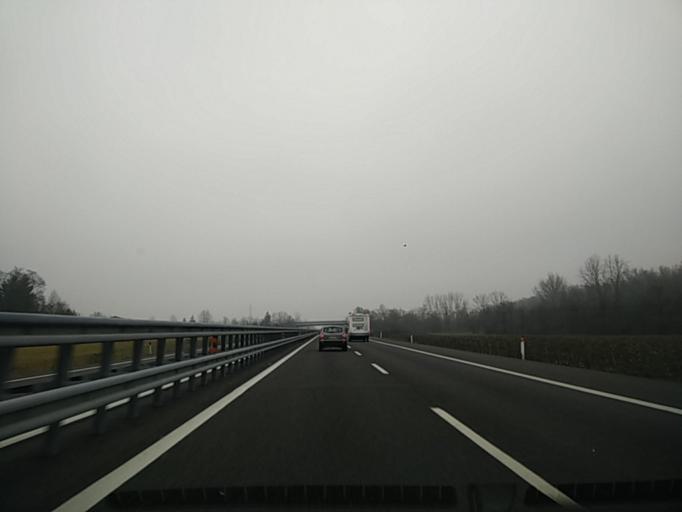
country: IT
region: Piedmont
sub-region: Provincia di Asti
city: Villafranca d'Asti
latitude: 44.9299
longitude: 8.0051
